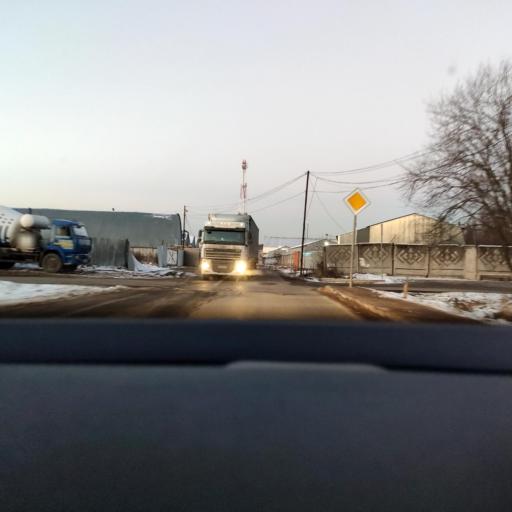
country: RU
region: Moskovskaya
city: Skhodnya
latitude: 55.8937
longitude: 37.3052
